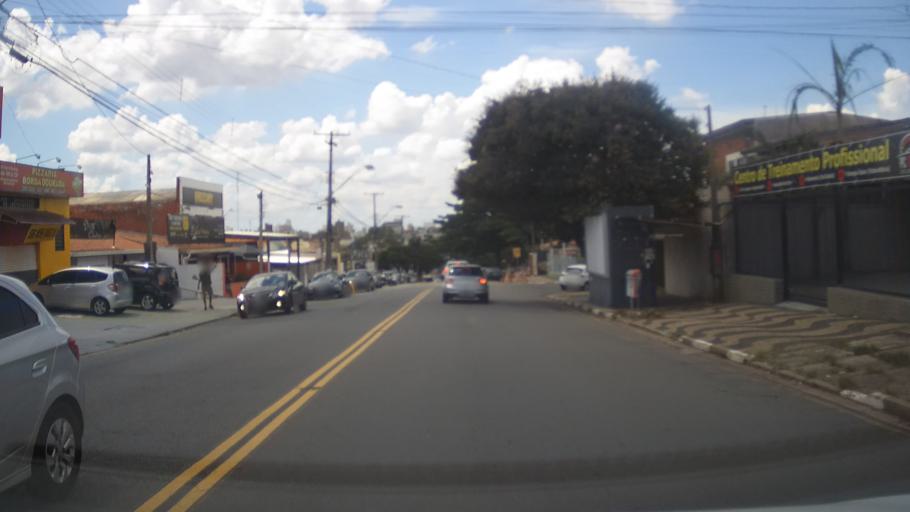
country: BR
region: Sao Paulo
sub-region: Campinas
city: Campinas
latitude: -22.9216
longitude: -47.0406
